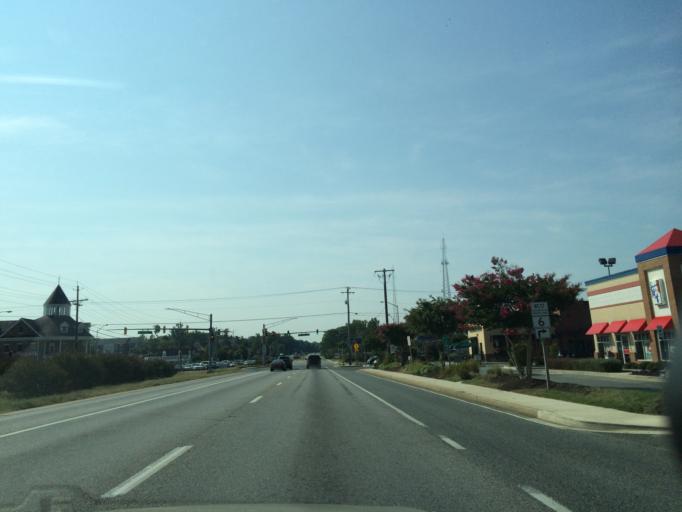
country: US
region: Maryland
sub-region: Charles County
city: La Plata
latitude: 38.5302
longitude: -76.9831
